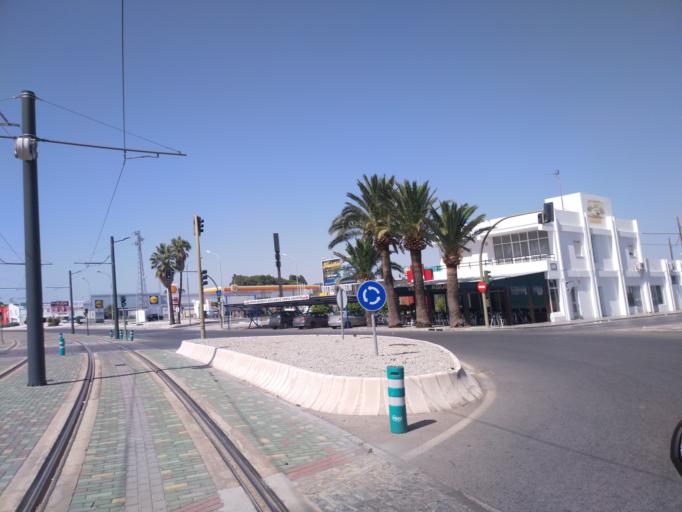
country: ES
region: Andalusia
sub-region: Provincia de Cadiz
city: Chiclana de la Frontera
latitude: 36.4294
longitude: -6.1431
